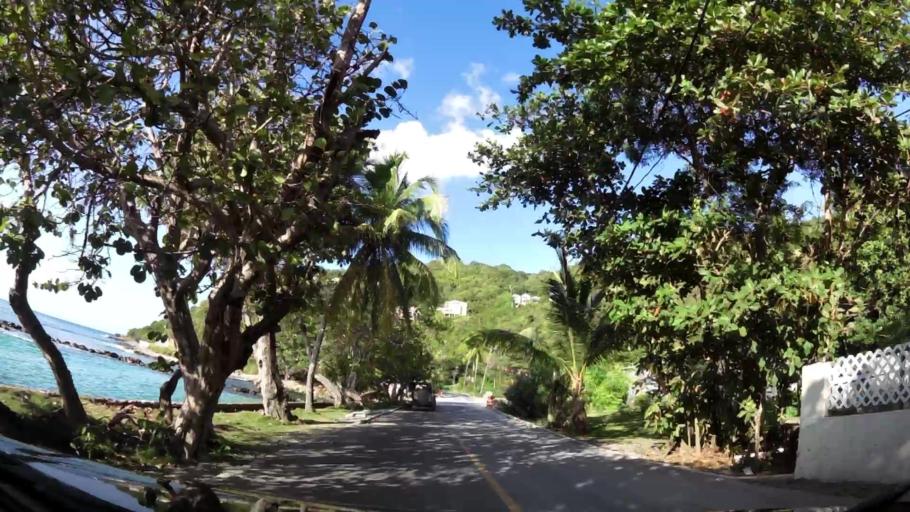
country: VG
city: Road Town
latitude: 18.4127
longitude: -64.6708
